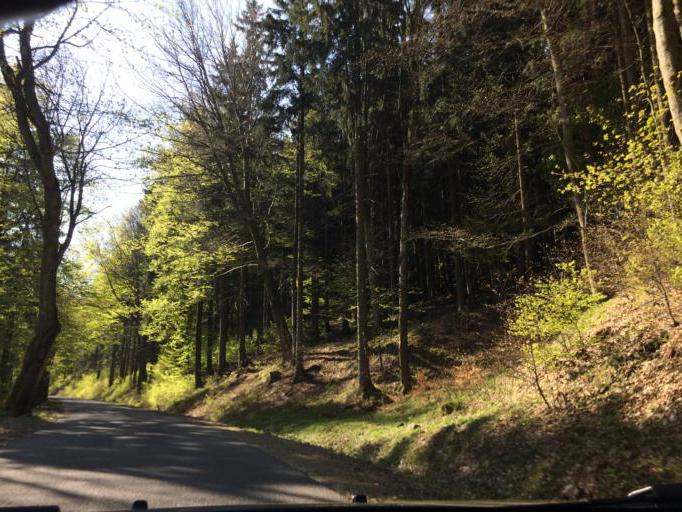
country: PL
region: Lower Silesian Voivodeship
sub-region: Powiat klodzki
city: Jugow
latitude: 50.6687
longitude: 16.5174
